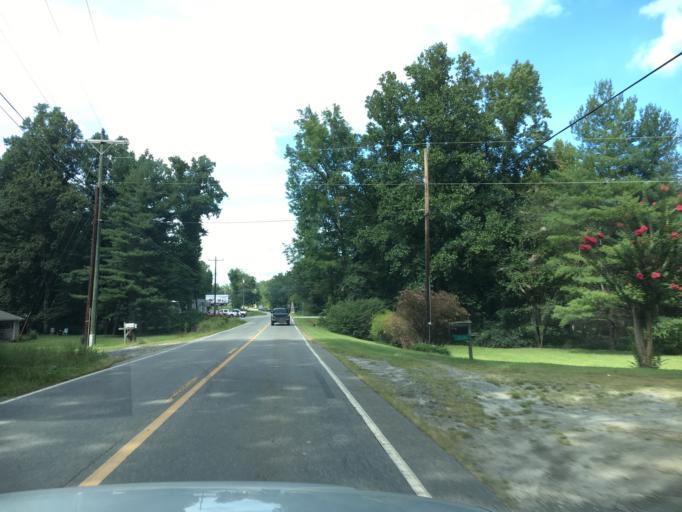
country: US
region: North Carolina
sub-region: Polk County
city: Columbus
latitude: 35.2767
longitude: -82.1807
